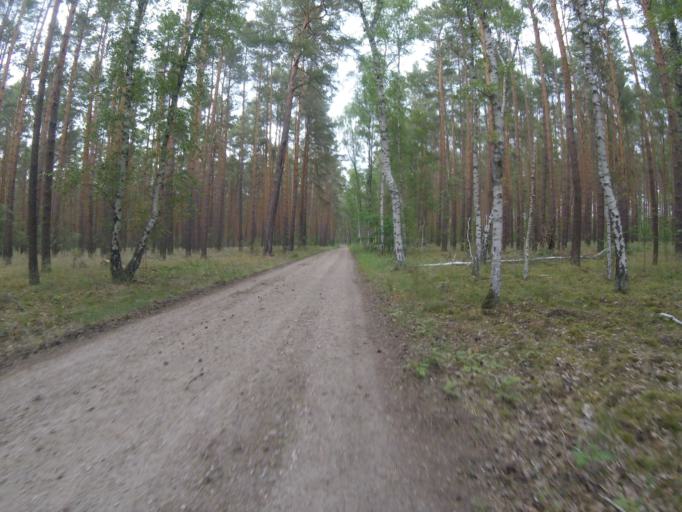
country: DE
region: Brandenburg
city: Gross Koris
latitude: 52.2036
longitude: 13.6983
